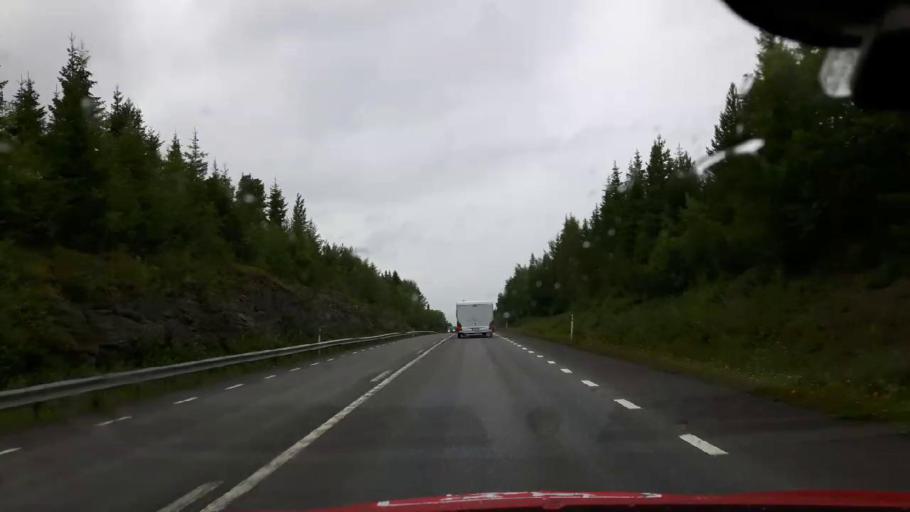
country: SE
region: Jaemtland
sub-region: Are Kommun
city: Jarpen
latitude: 63.3211
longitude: 13.5528
